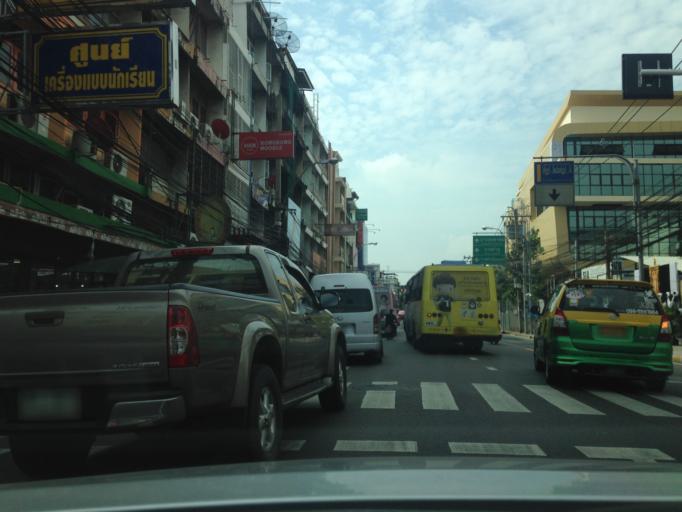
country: TH
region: Bangkok
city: Phra Nakhon
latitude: 13.7707
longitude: 100.5046
